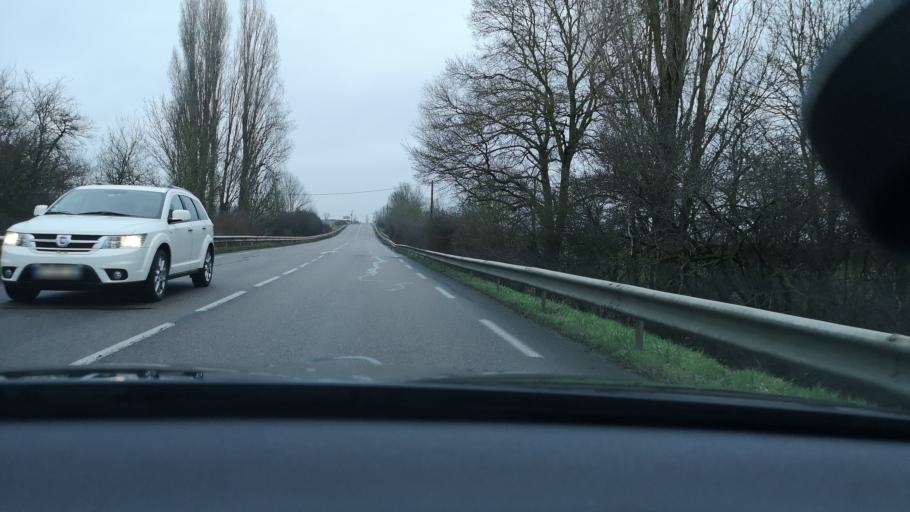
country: FR
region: Bourgogne
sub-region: Departement de la Cote-d'Or
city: Seurre
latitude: 46.9431
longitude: 5.1528
